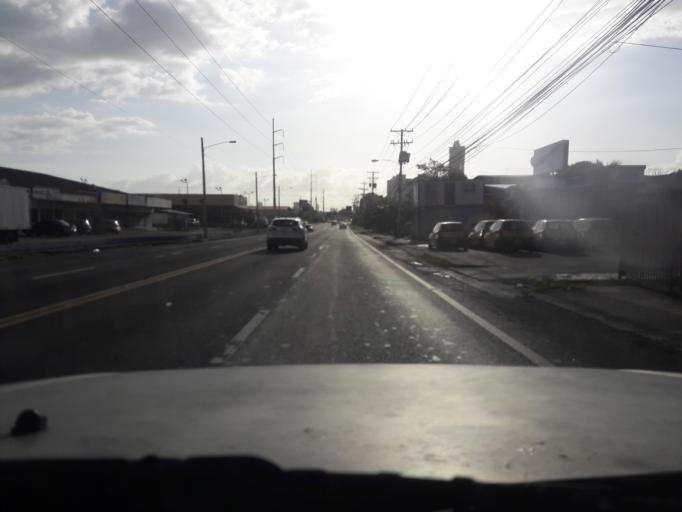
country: PA
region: Panama
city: San Miguelito
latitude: 9.0295
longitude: -79.4778
